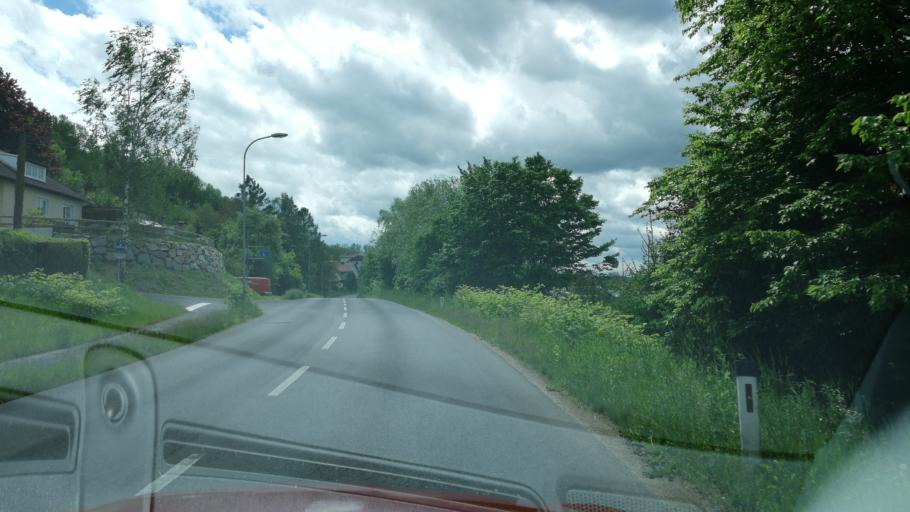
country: AT
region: Upper Austria
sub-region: Politischer Bezirk Linz-Land
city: Ansfelden
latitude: 48.2025
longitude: 14.2720
